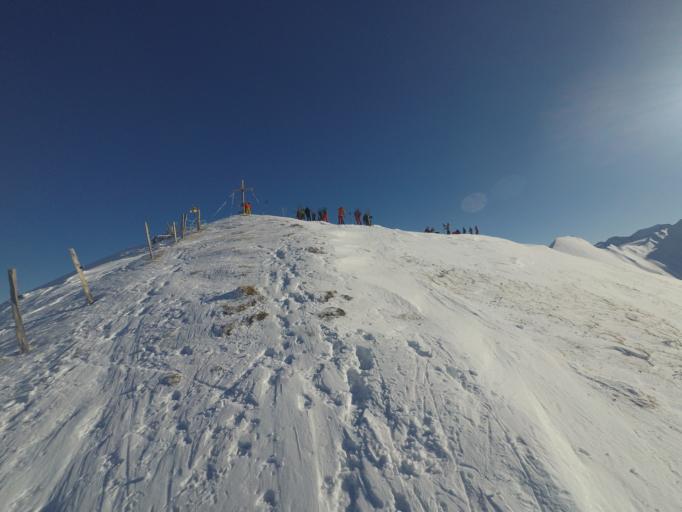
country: AT
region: Salzburg
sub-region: Politischer Bezirk Sankt Johann im Pongau
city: Huttschlag
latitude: 47.1738
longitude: 13.3064
